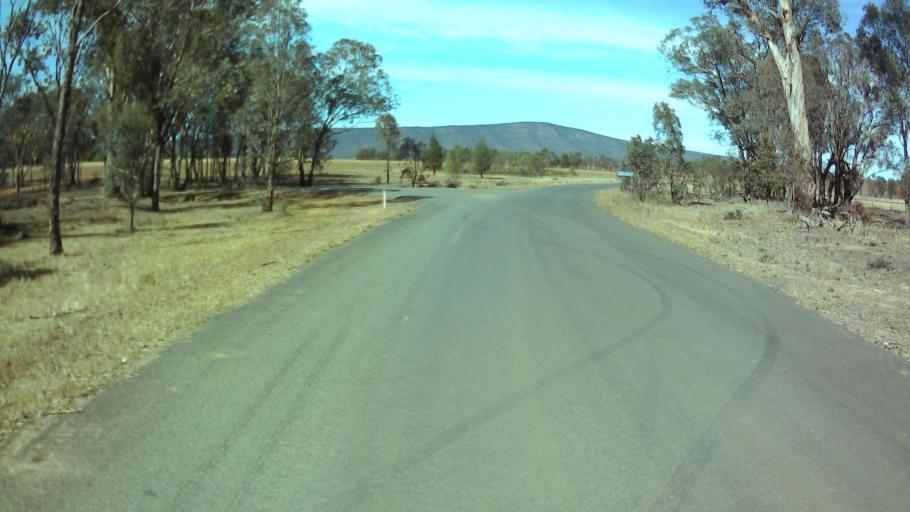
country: AU
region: New South Wales
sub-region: Weddin
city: Grenfell
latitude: -33.9401
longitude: 148.0786
